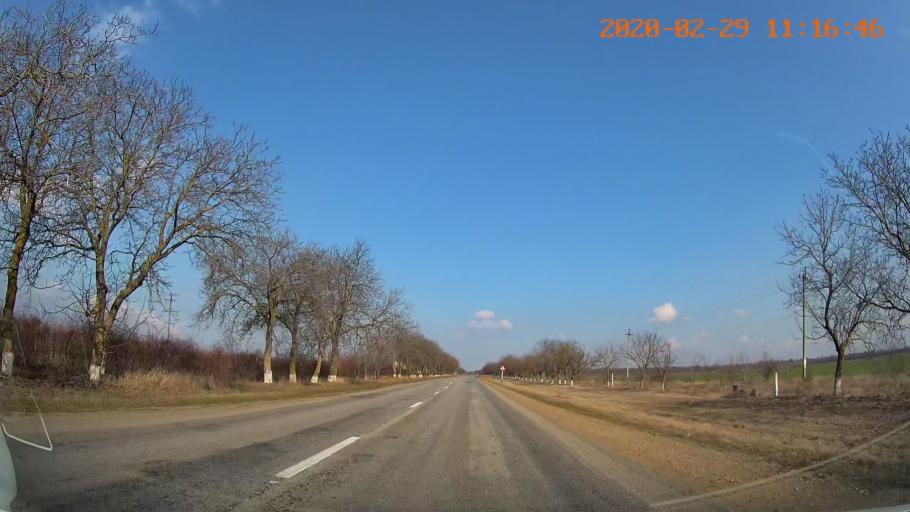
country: MD
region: Telenesti
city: Dubasari
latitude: 47.3133
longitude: 29.1687
